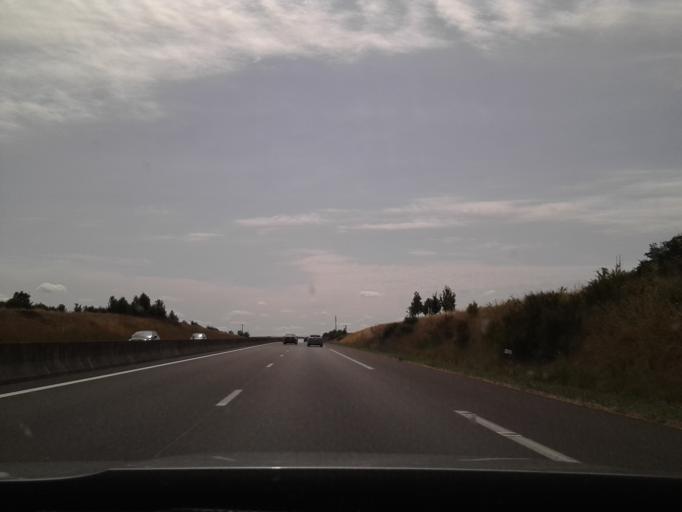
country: FR
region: Centre
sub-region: Departement d'Indre-et-Loire
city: Saint-Christophe-sur-le-Nais
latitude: 47.6243
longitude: 0.5136
